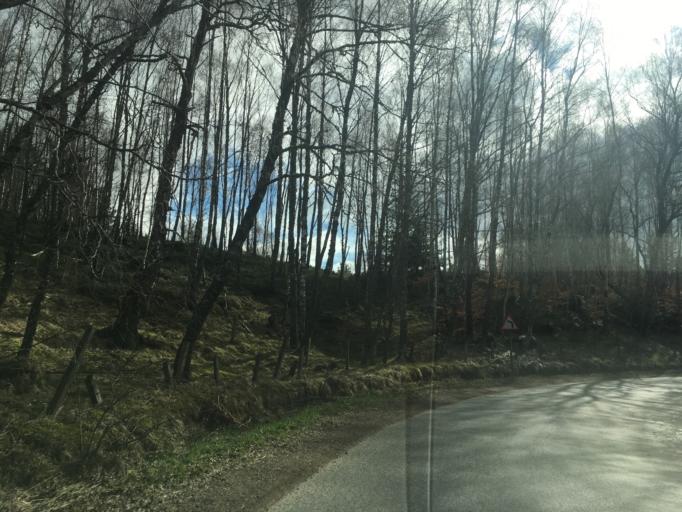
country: GB
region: Scotland
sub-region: Highland
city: Aviemore
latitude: 57.1689
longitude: -3.8263
